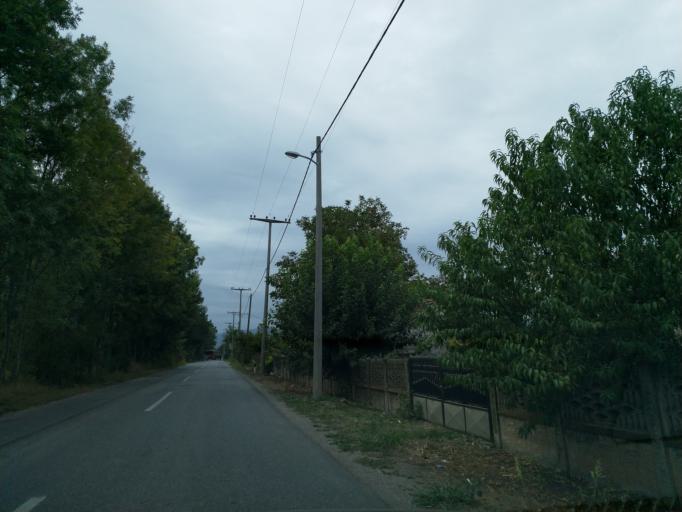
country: RS
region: Central Serbia
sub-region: Pomoravski Okrug
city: Paracin
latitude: 43.8503
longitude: 21.3878
